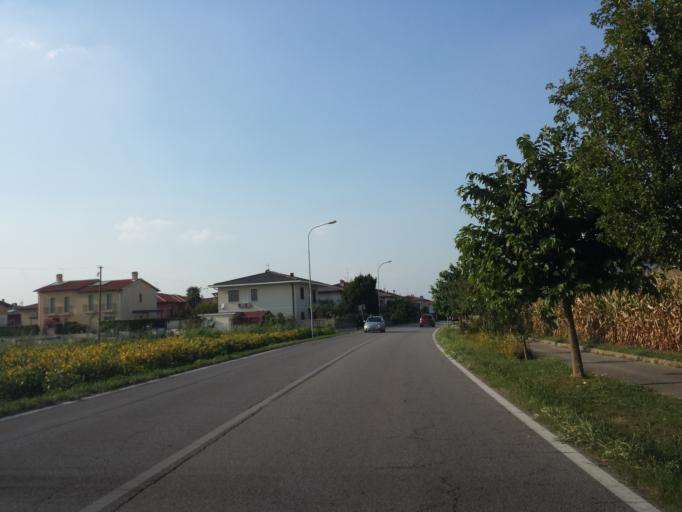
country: IT
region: Veneto
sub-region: Provincia di Vicenza
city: Marola
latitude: 45.5300
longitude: 11.6311
